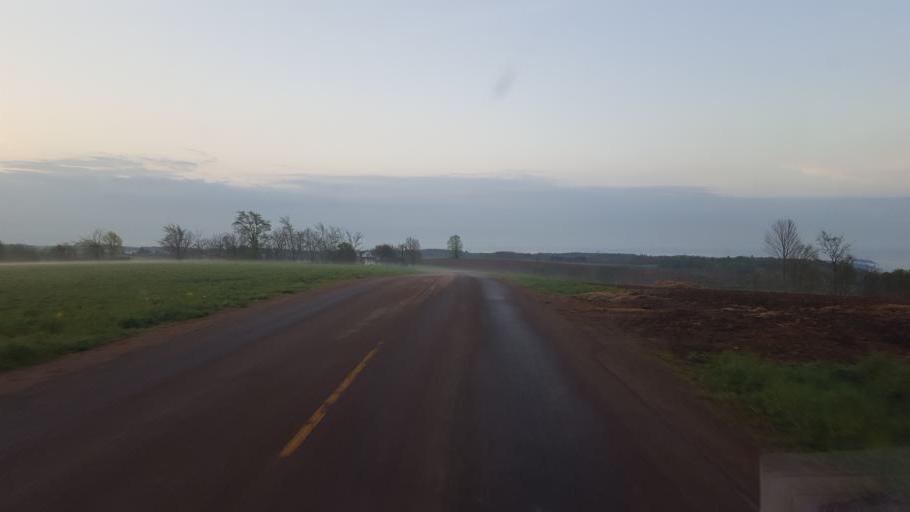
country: US
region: Wisconsin
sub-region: Vernon County
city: Hillsboro
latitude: 43.6088
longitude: -90.4373
